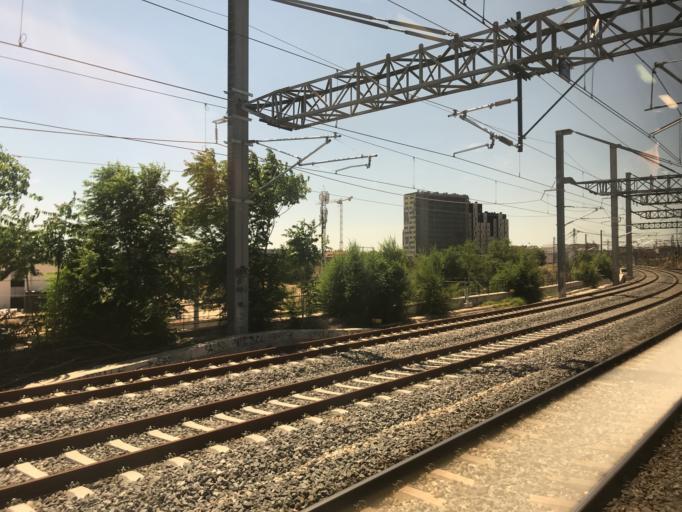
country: ES
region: Madrid
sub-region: Provincia de Madrid
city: Retiro
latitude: 40.4001
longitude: -3.6789
